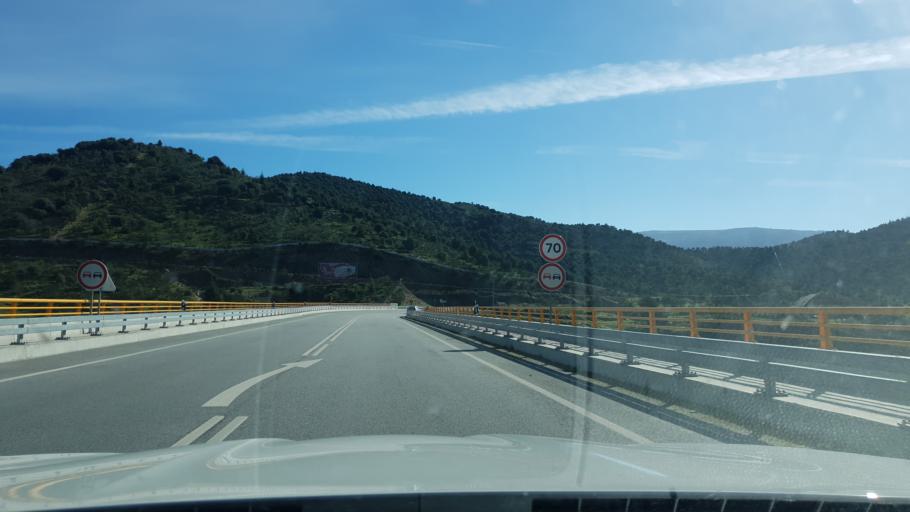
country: PT
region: Braganca
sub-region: Torre de Moncorvo
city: Torre de Moncorvo
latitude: 41.2099
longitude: -7.0835
